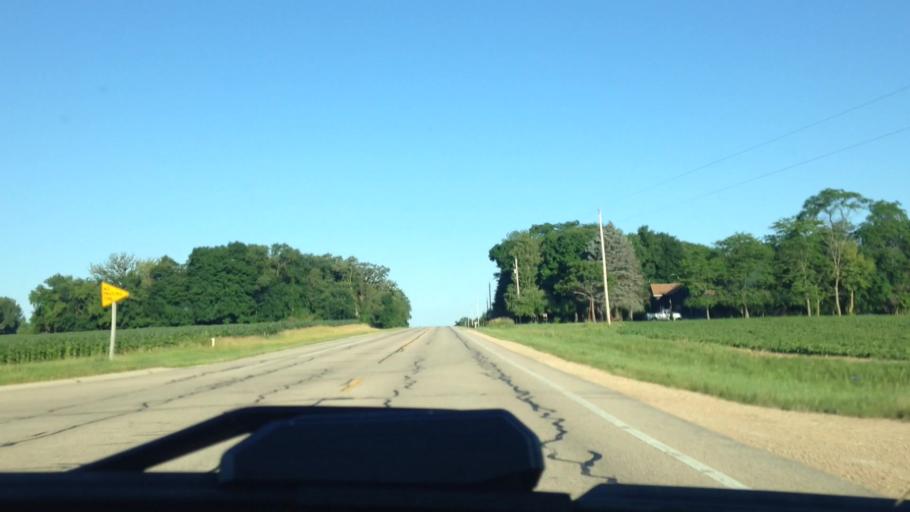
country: US
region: Wisconsin
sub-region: Columbia County
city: Fall River
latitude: 43.3415
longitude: -89.0688
